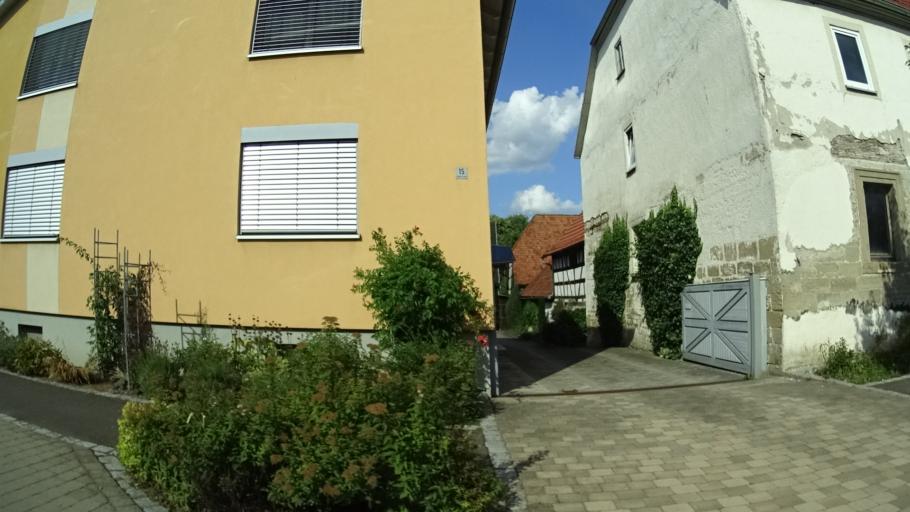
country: DE
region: Bavaria
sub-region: Regierungsbezirk Unterfranken
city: Bundorf
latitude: 50.2731
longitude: 10.5254
